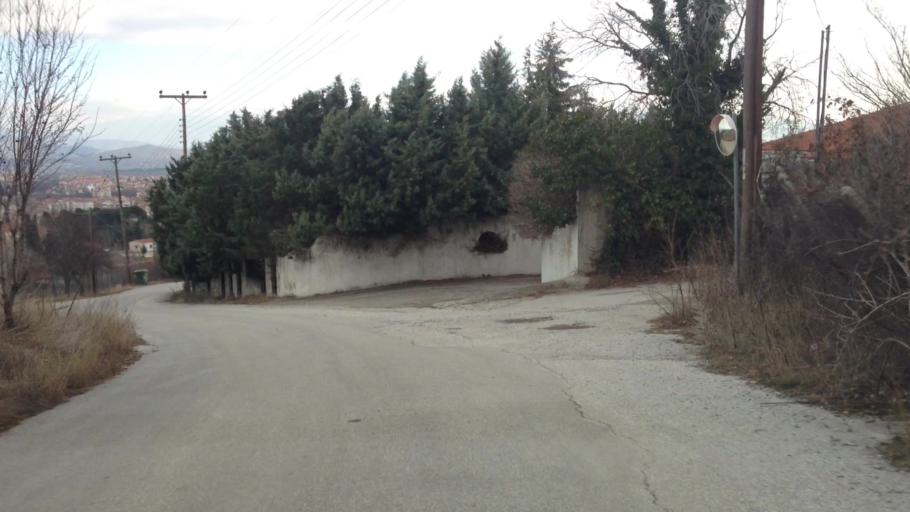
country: GR
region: West Macedonia
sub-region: Nomos Kozanis
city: Kozani
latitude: 40.2921
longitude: 21.7712
